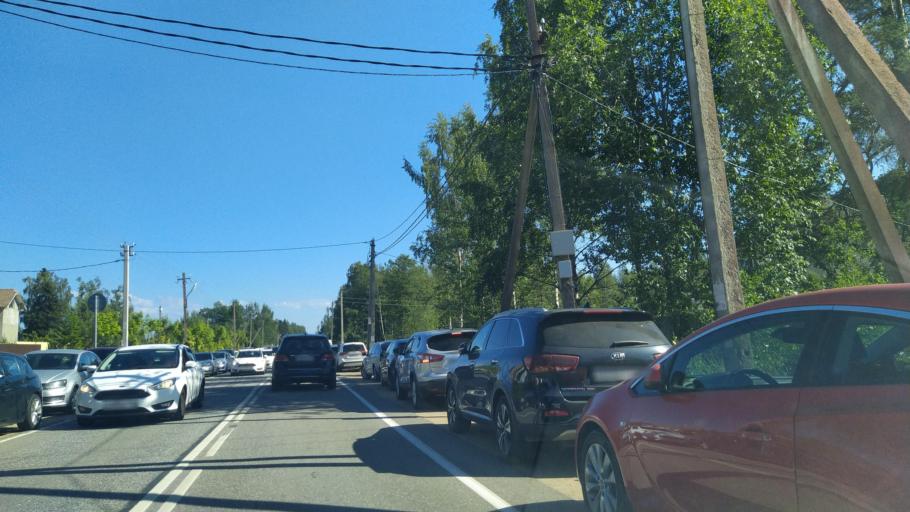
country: RU
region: Leningrad
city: Borisova Griva
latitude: 60.1189
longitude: 31.0767
